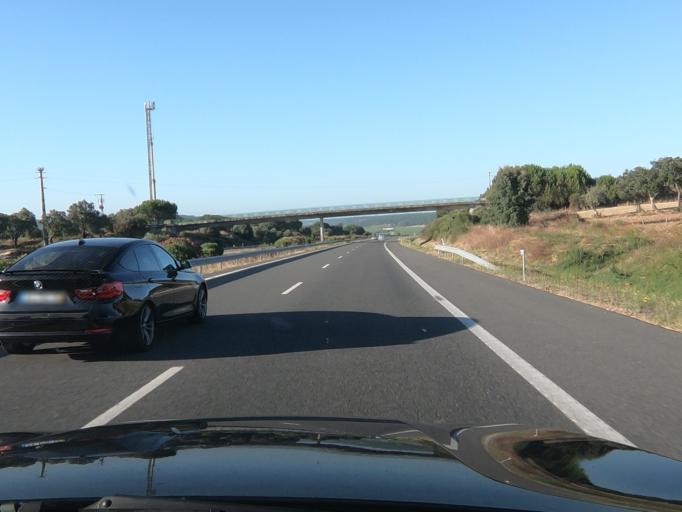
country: PT
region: Setubal
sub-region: Alcacer do Sal
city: Alcacer do Sal
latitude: 38.3750
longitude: -8.4871
